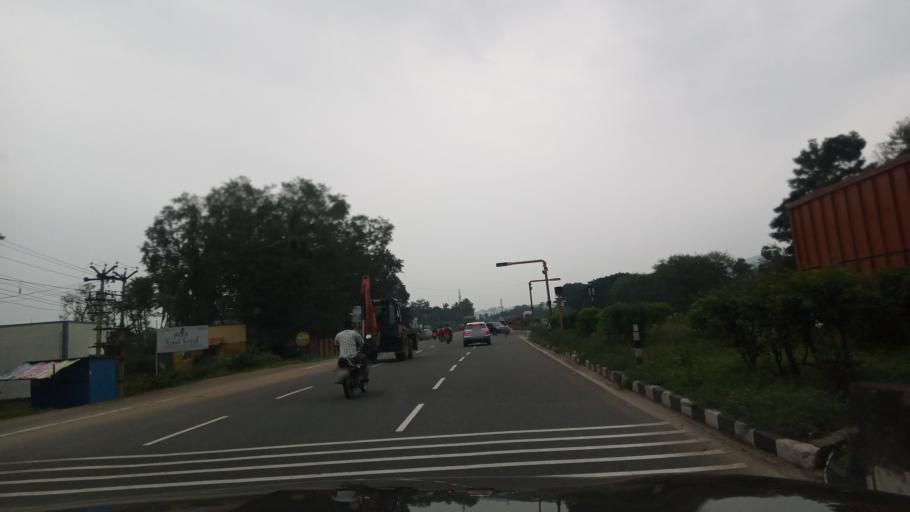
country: IN
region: Tamil Nadu
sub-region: Vellore
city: Katpadi
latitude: 12.9465
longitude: 79.2249
